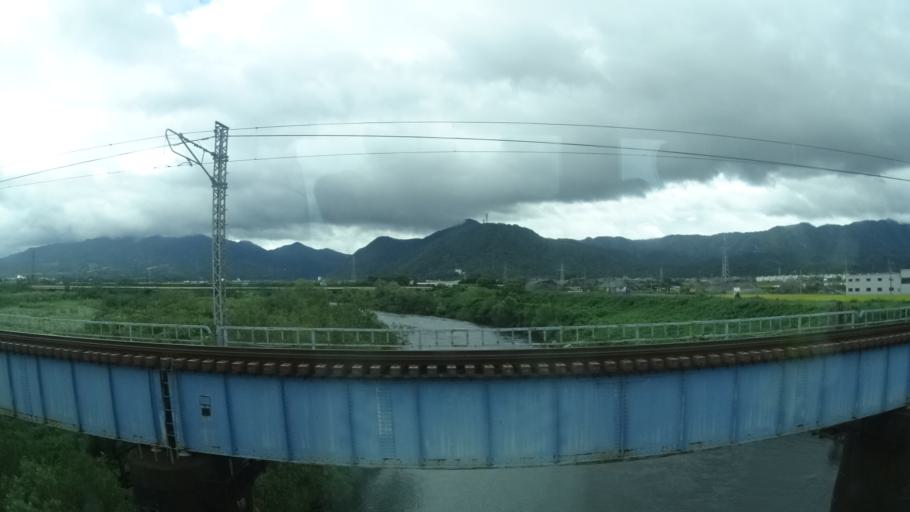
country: JP
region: Niigata
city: Shibata
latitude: 38.0713
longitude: 139.4122
